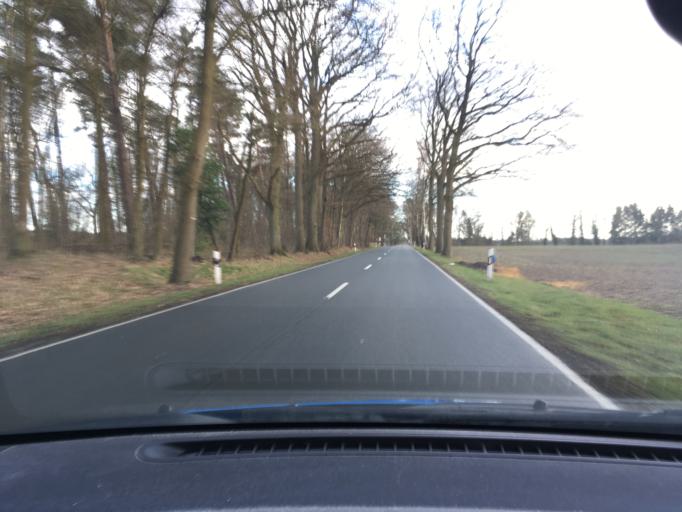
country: DE
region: Lower Saxony
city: Hanstedt
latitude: 53.2234
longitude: 10.0252
